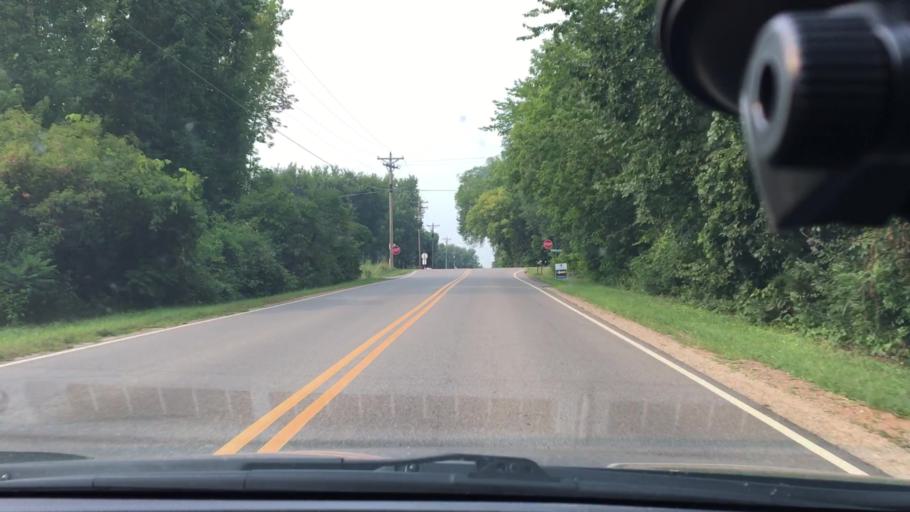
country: US
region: Minnesota
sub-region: Hennepin County
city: Champlin
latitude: 45.2068
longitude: -93.4427
